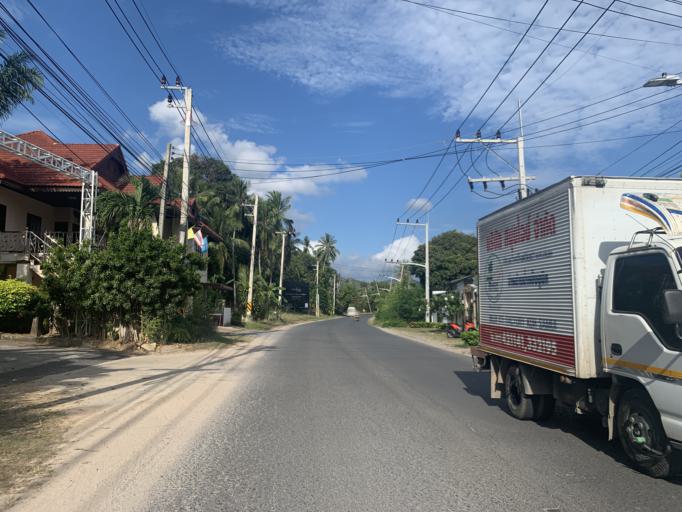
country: TH
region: Surat Thani
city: Ko Samui
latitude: 9.5606
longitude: 100.0385
